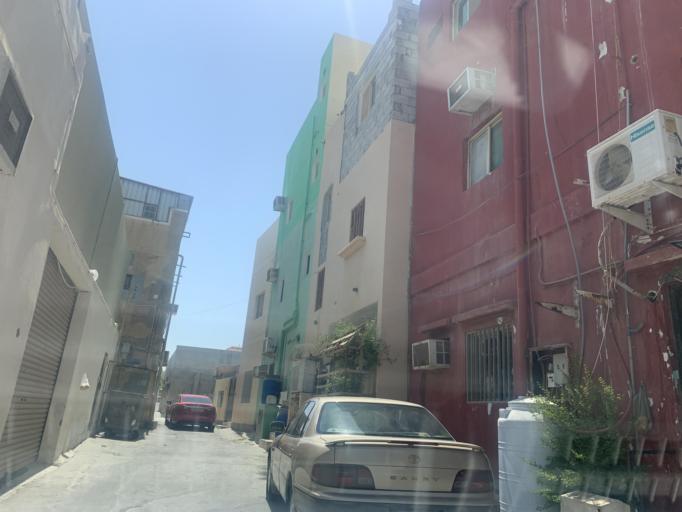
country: BH
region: Muharraq
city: Al Muharraq
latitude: 26.2839
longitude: 50.6263
